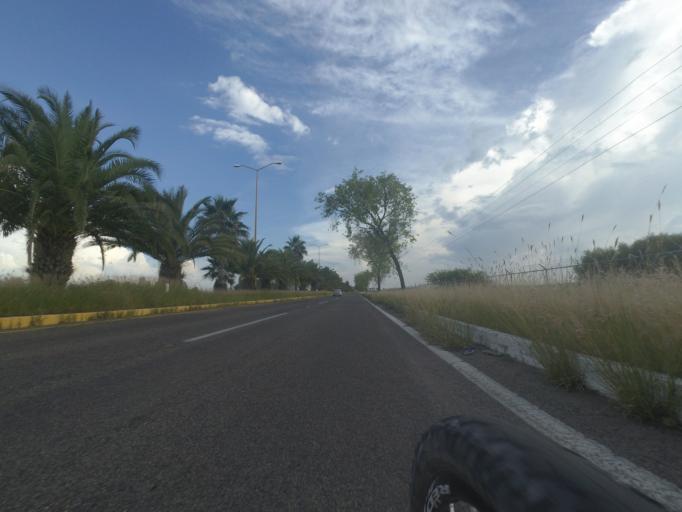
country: MX
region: Aguascalientes
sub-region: Aguascalientes
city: Penuelas (El Cienegal)
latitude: 21.7147
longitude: -102.3105
